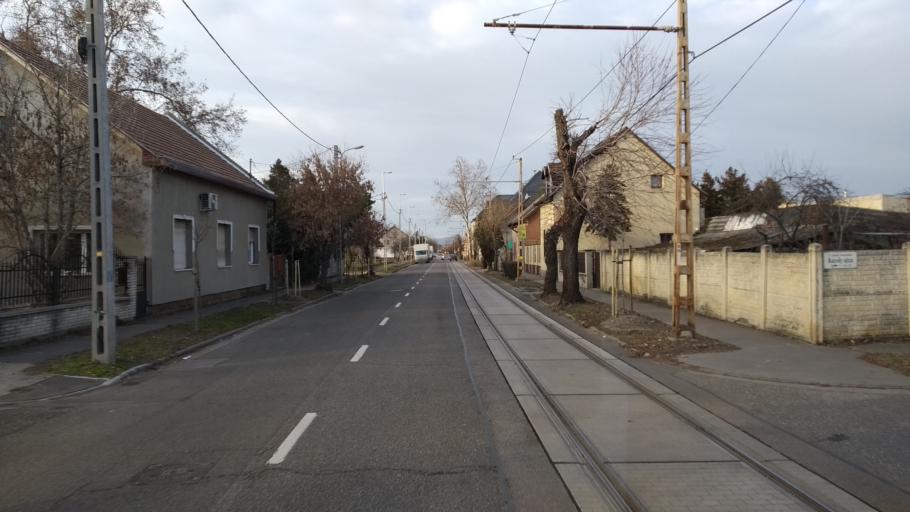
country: HU
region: Budapest
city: Budapest XX. keruelet
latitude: 47.4259
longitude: 19.1217
